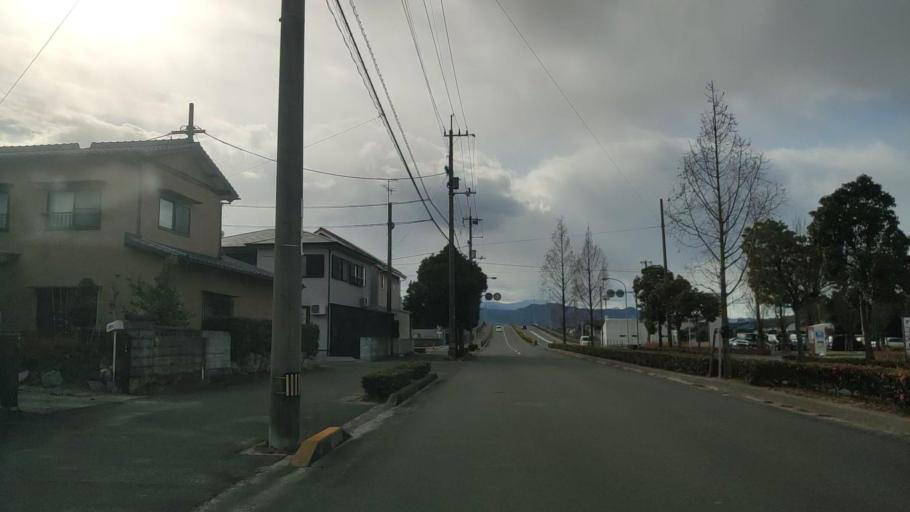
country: JP
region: Ehime
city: Saijo
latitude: 34.0468
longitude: 133.0075
